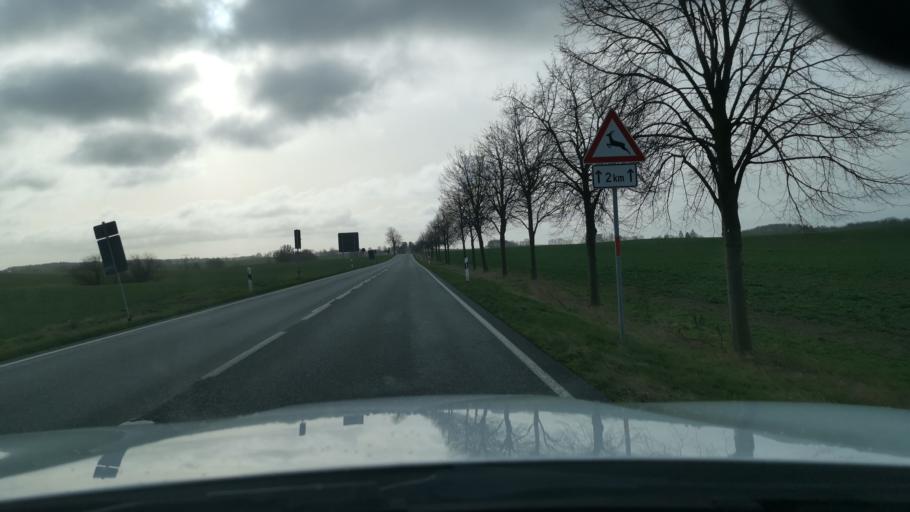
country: DE
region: Mecklenburg-Vorpommern
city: Dummerstorf
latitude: 53.9715
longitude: 12.2867
